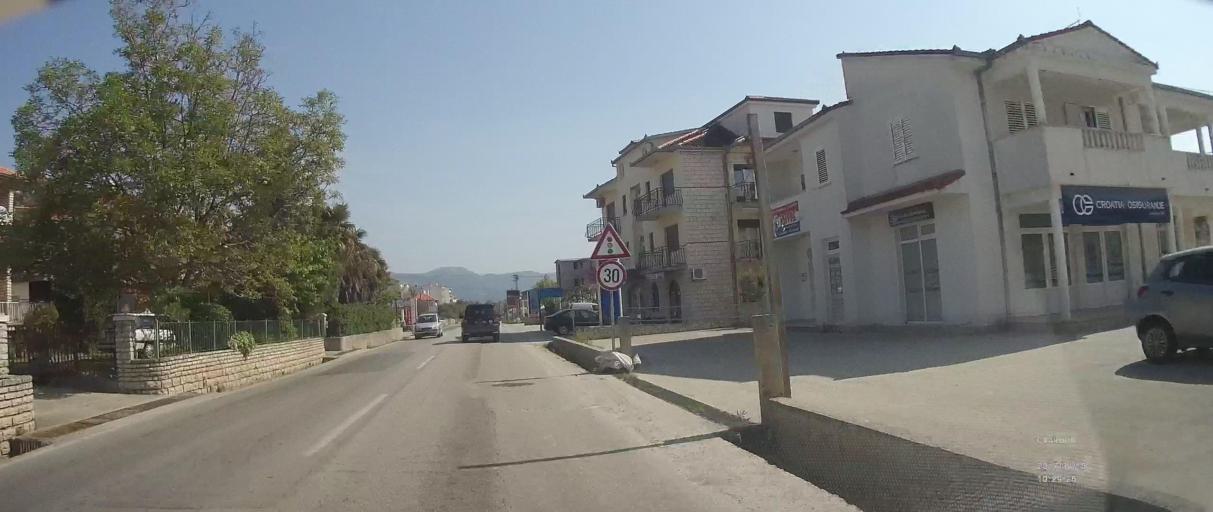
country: HR
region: Splitsko-Dalmatinska
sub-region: Grad Trogir
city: Trogir
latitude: 43.5240
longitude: 16.2665
